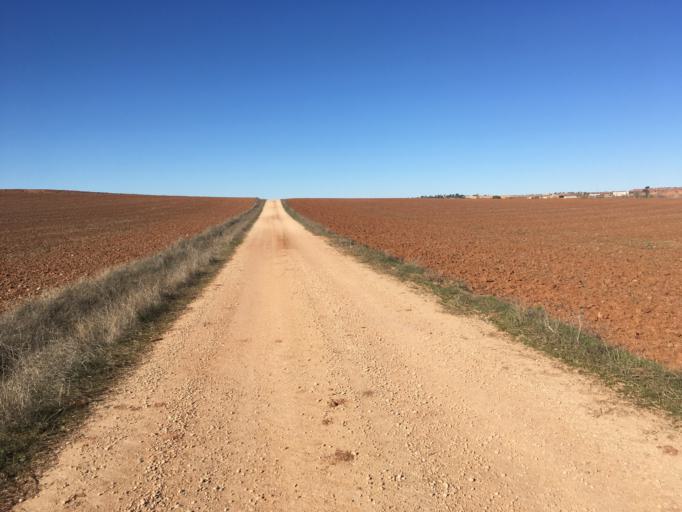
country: ES
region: Castille-La Mancha
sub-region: Provincia de Cuenca
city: Atalaya del Canavate
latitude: 39.5410
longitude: -2.2418
